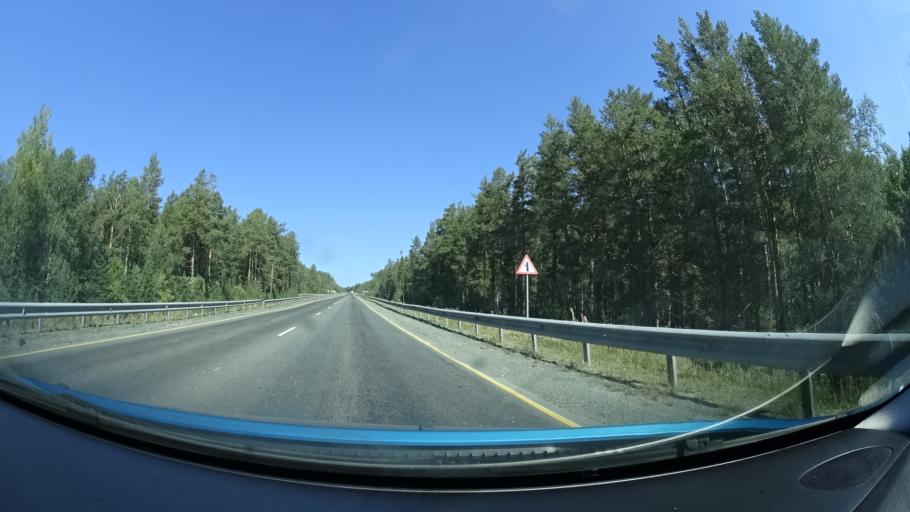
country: RU
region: Bashkortostan
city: Abzakovo
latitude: 53.8788
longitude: 58.5324
